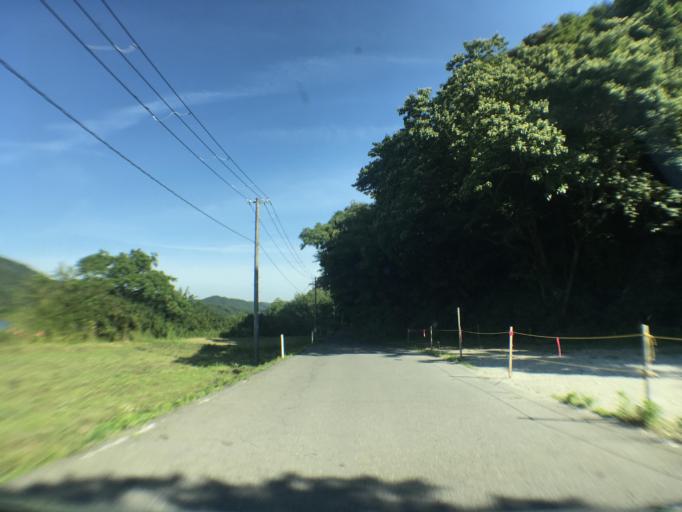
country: JP
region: Miyagi
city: Wakuya
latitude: 38.6342
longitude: 141.2848
